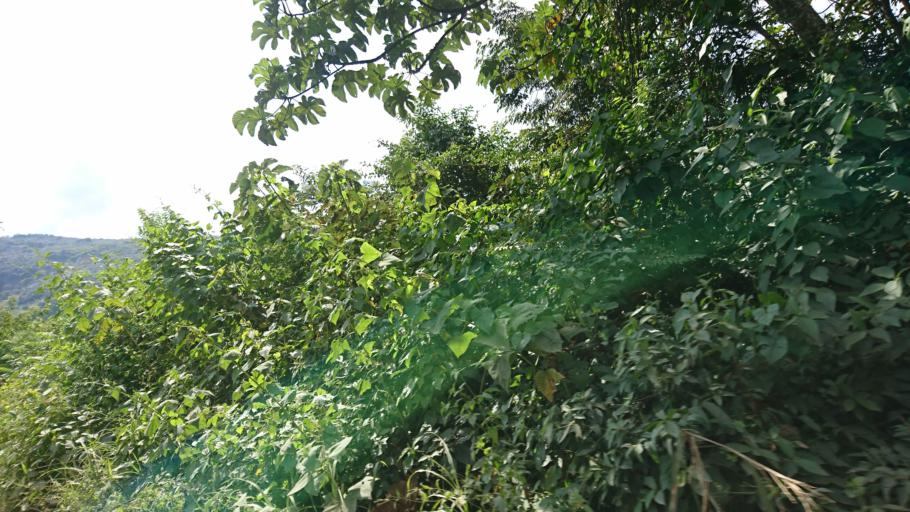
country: BO
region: La Paz
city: Coroico
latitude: -16.0858
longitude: -67.7855
